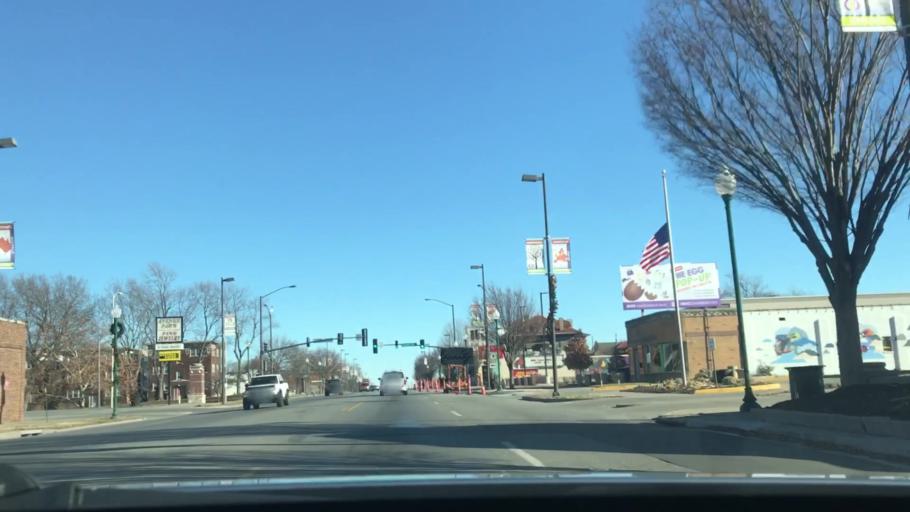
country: US
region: Missouri
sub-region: Clay County
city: North Kansas City
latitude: 39.1062
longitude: -94.5495
